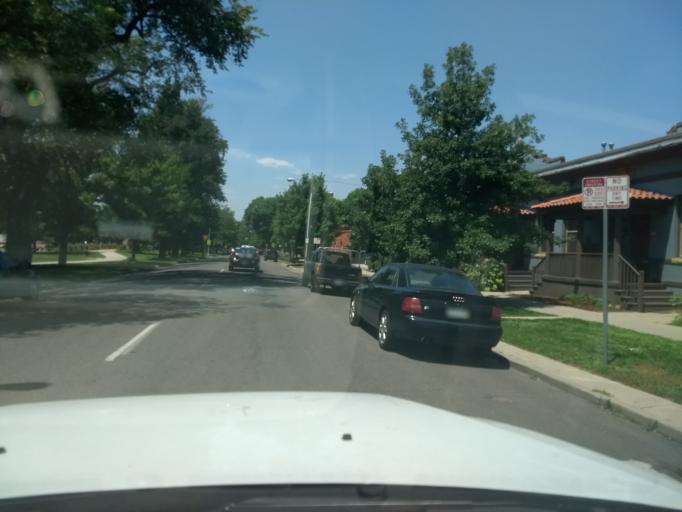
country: US
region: Colorado
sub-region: Denver County
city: Denver
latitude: 39.7620
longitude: -104.9661
